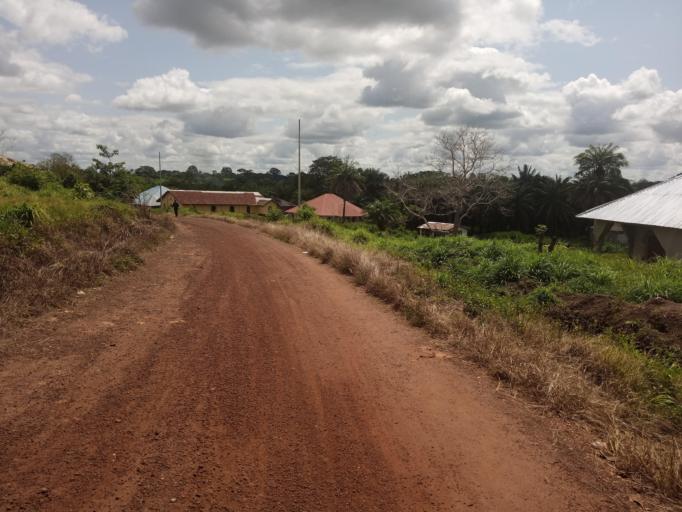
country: SL
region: Northern Province
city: Kamakwie
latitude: 9.4938
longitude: -12.2449
